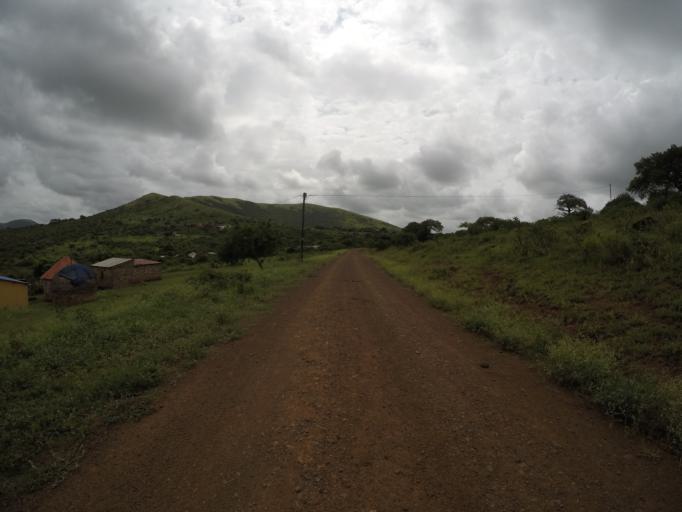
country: ZA
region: KwaZulu-Natal
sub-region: uThungulu District Municipality
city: Empangeni
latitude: -28.6147
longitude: 31.8956
